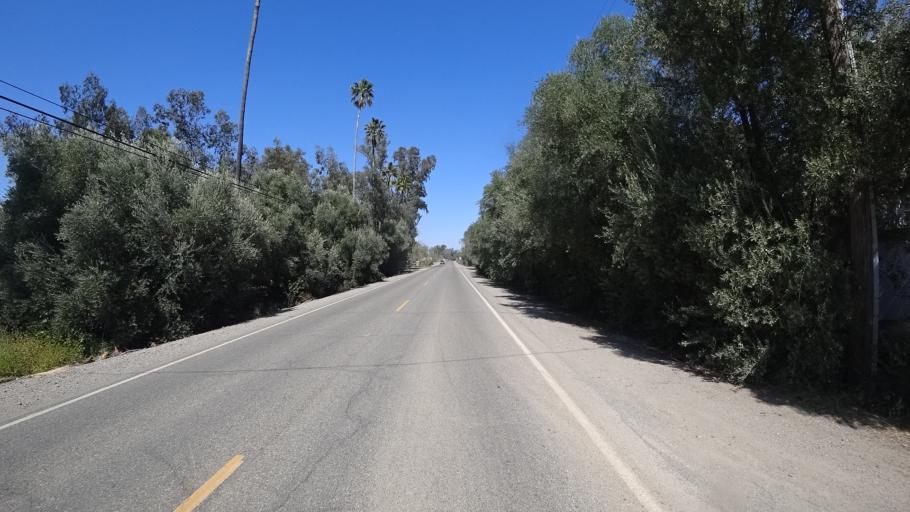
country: US
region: California
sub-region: Glenn County
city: Orland
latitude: 39.7071
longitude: -122.1969
